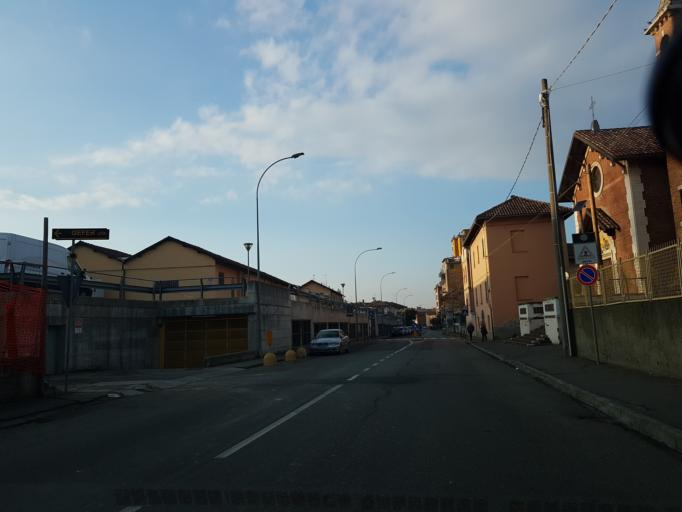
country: IT
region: Piedmont
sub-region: Provincia di Alessandria
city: Novi Ligure
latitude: 44.7576
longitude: 8.7989
